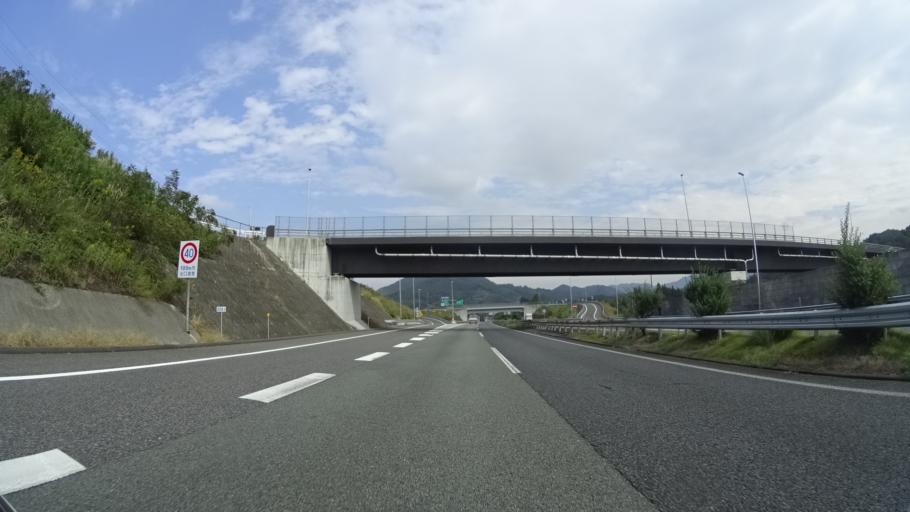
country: JP
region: Kumamoto
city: Matsubase
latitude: 32.5755
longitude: 130.7087
